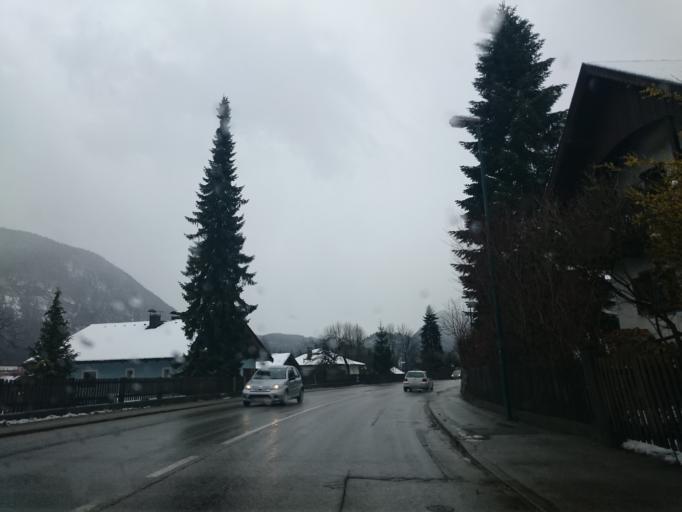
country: AT
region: Tyrol
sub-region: Politischer Bezirk Kufstein
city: Kufstein
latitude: 47.5811
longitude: 12.1629
